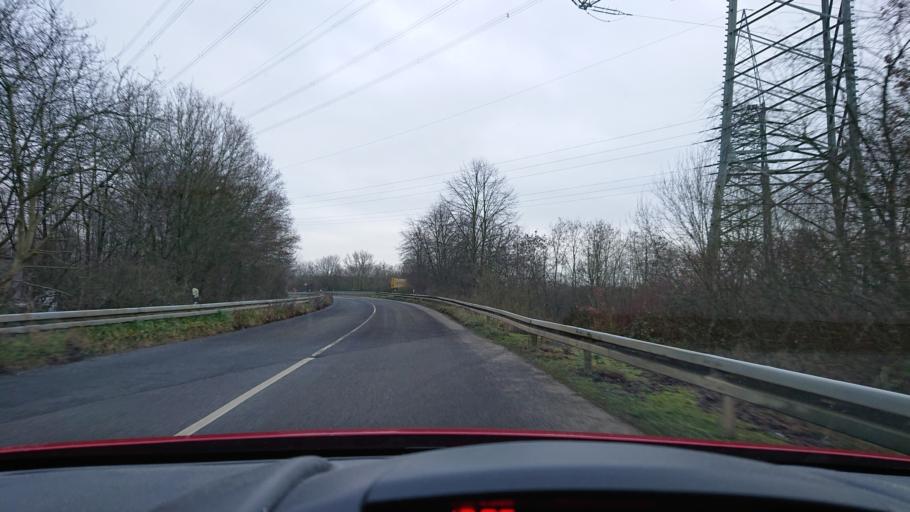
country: DE
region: North Rhine-Westphalia
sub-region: Regierungsbezirk Koln
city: Bergheim
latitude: 50.9767
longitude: 6.6638
